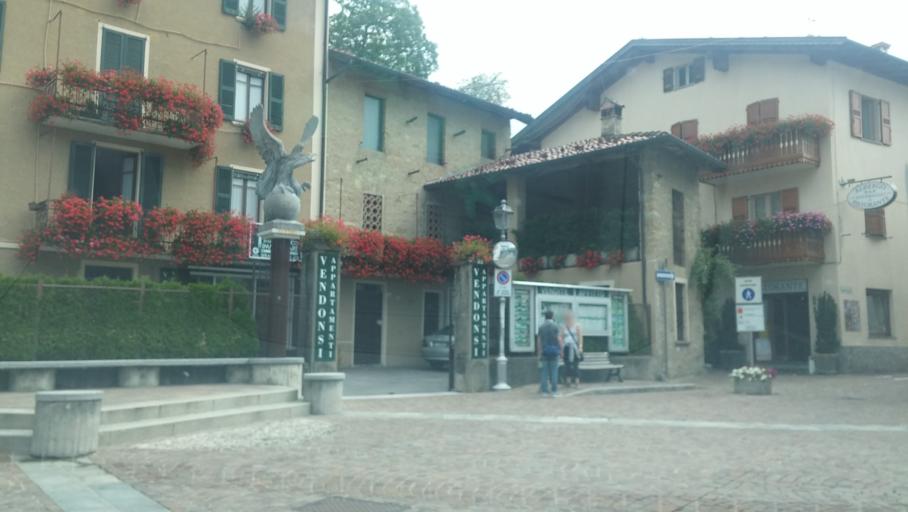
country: IT
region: Lombardy
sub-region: Provincia di Lecco
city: Moggio
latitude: 45.9328
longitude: 9.4856
